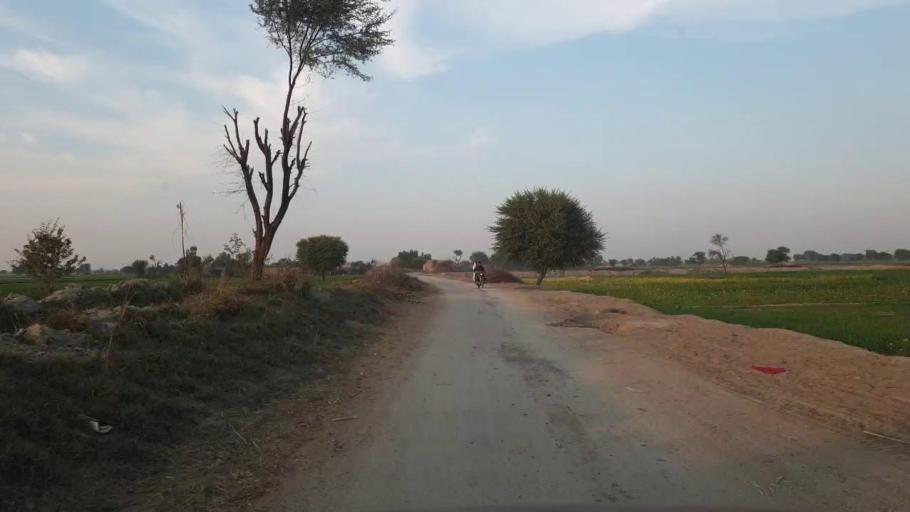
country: PK
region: Sindh
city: Shahpur Chakar
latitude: 26.1925
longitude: 68.6173
